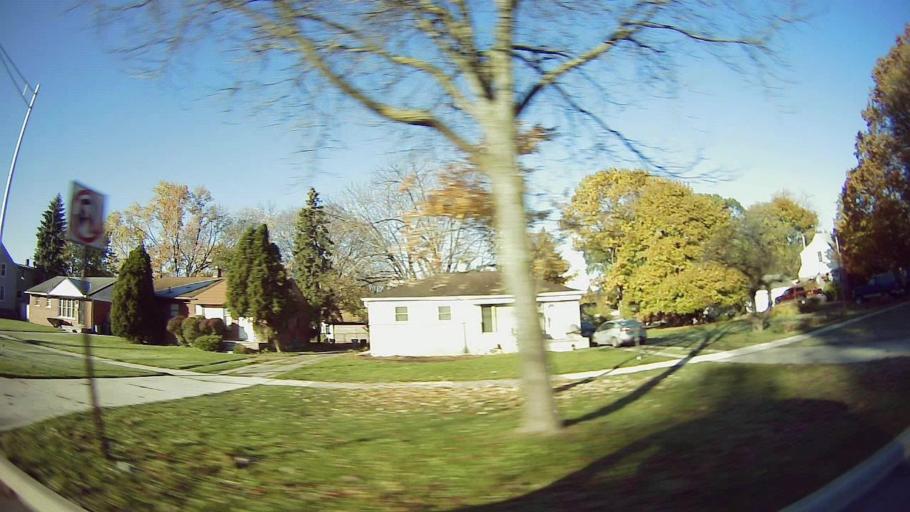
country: US
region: Michigan
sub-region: Oakland County
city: Oak Park
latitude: 42.4691
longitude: -83.1825
